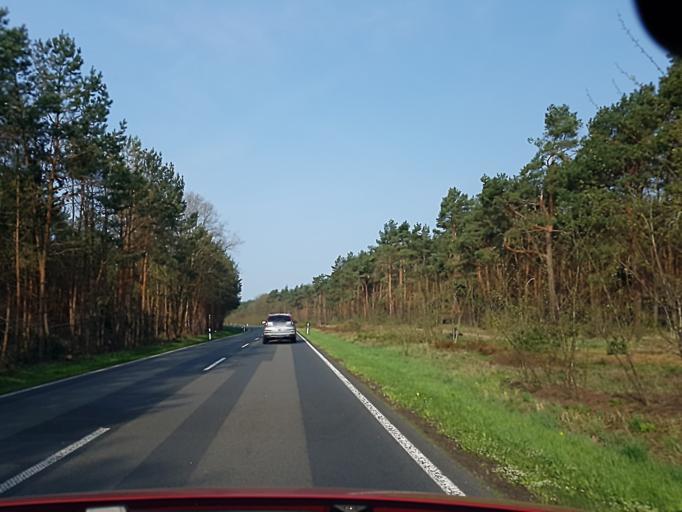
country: DE
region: Saxony
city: Beilrode
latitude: 51.5901
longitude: 13.0916
